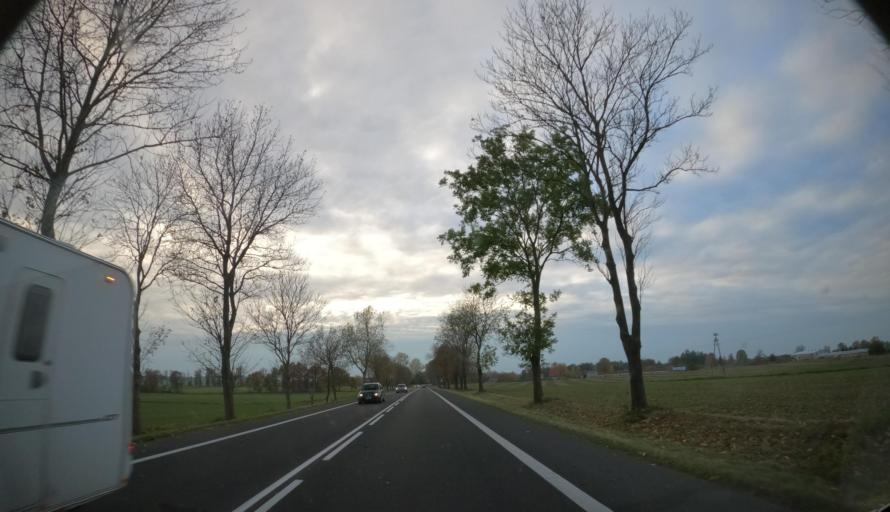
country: PL
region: West Pomeranian Voivodeship
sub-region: Powiat slawienski
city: Slawno
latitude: 54.3384
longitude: 16.6386
